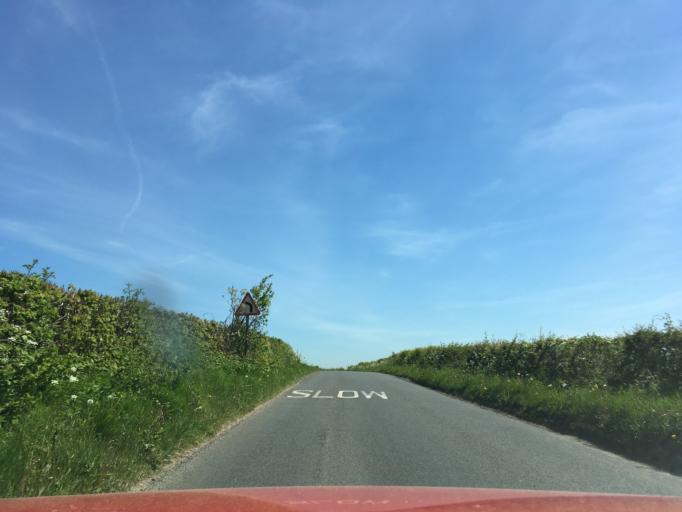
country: GB
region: England
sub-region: Gloucestershire
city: Coates
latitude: 51.7209
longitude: -2.0699
